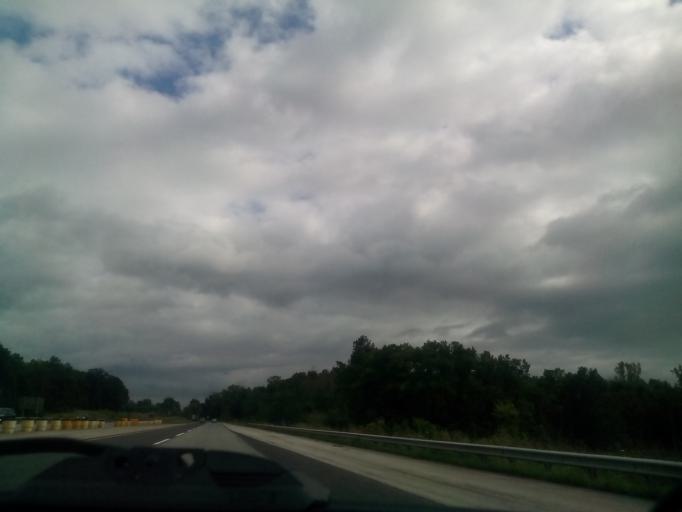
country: US
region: Indiana
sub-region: Steuben County
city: Fremont
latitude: 41.7228
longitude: -84.9641
